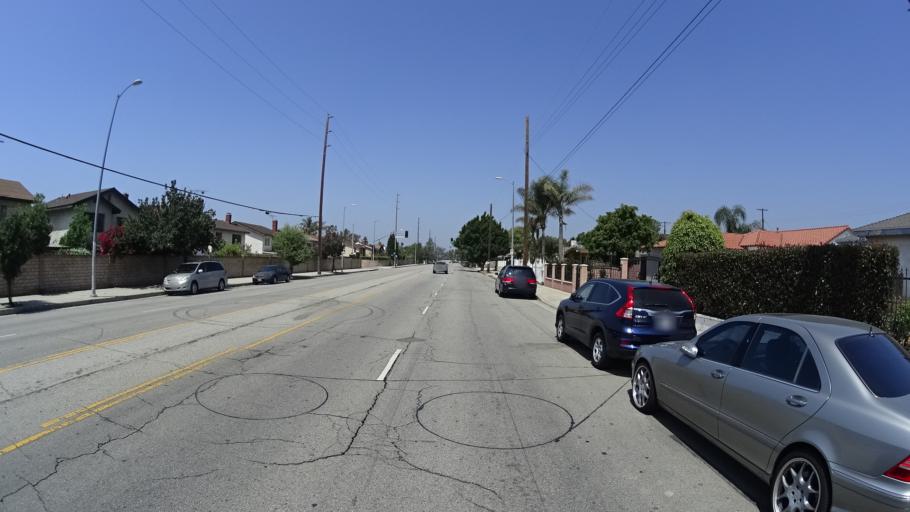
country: US
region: California
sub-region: Los Angeles County
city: North Hollywood
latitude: 34.2085
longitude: -118.4012
